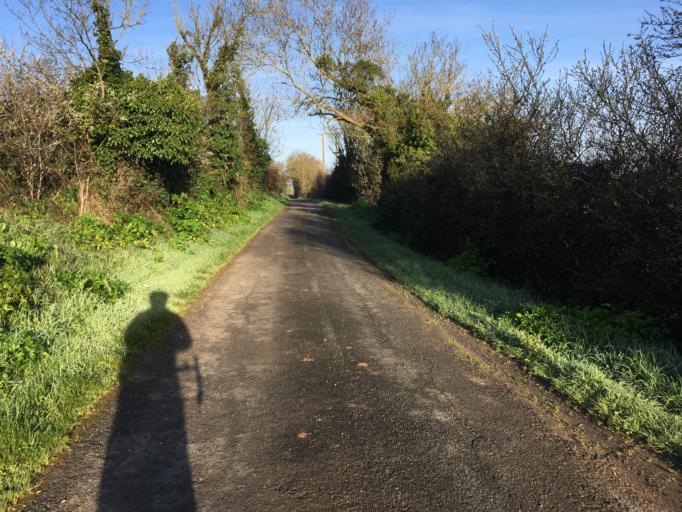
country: FR
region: Poitou-Charentes
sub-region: Departement de la Charente-Maritime
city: Nieul-sur-Mer
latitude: 46.1979
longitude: -1.1787
